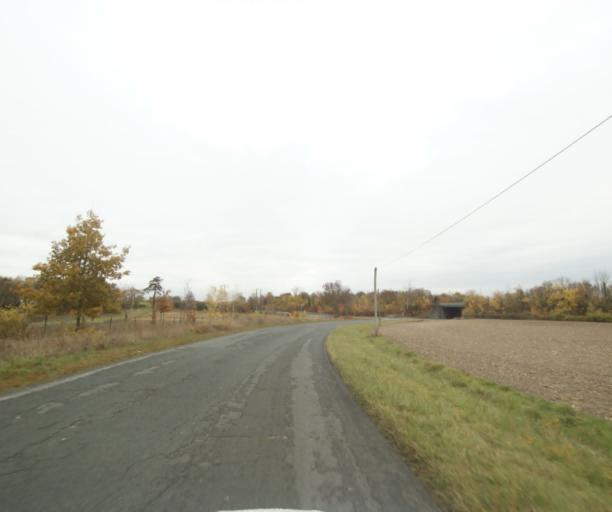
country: FR
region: Poitou-Charentes
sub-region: Departement de la Charente-Maritime
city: Chermignac
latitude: 45.7189
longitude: -0.6613
